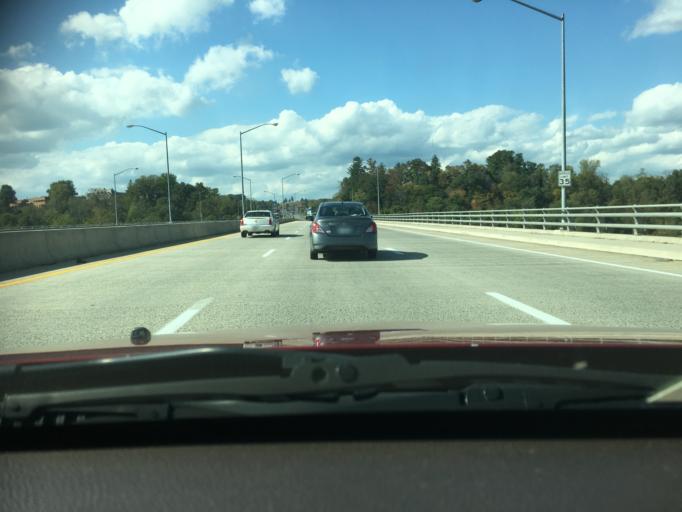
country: US
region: Virginia
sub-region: City of Radford
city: Radford
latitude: 37.1374
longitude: -80.5724
